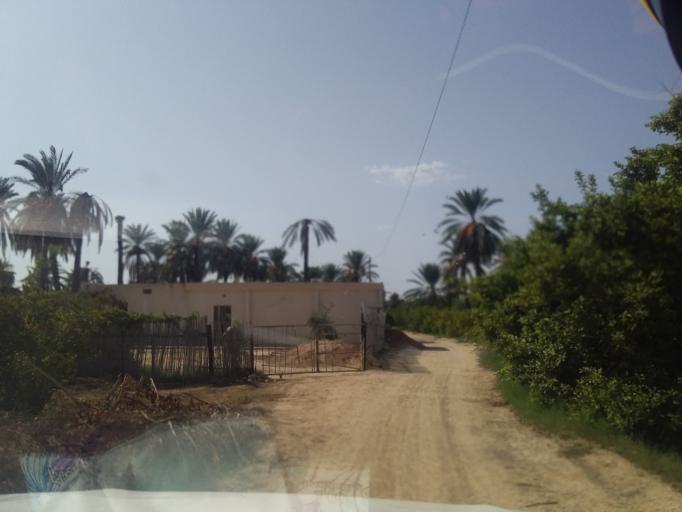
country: TN
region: Qabis
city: Gabes
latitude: 33.6279
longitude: 10.2905
